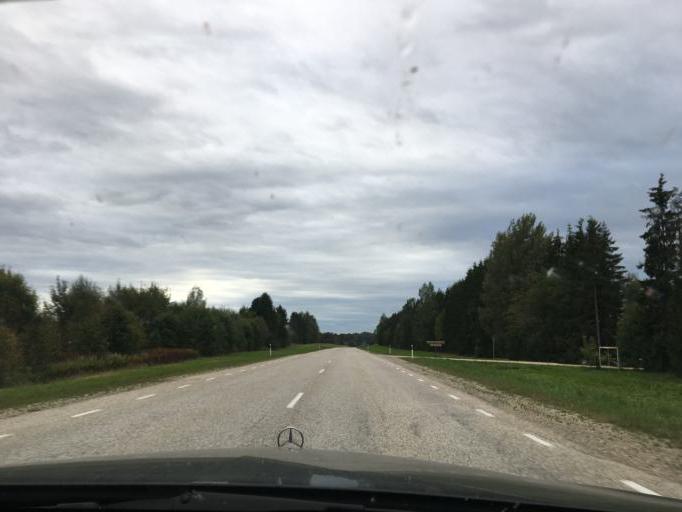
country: LV
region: Aluksnes Rajons
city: Aluksne
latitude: 57.6160
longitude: 27.2660
